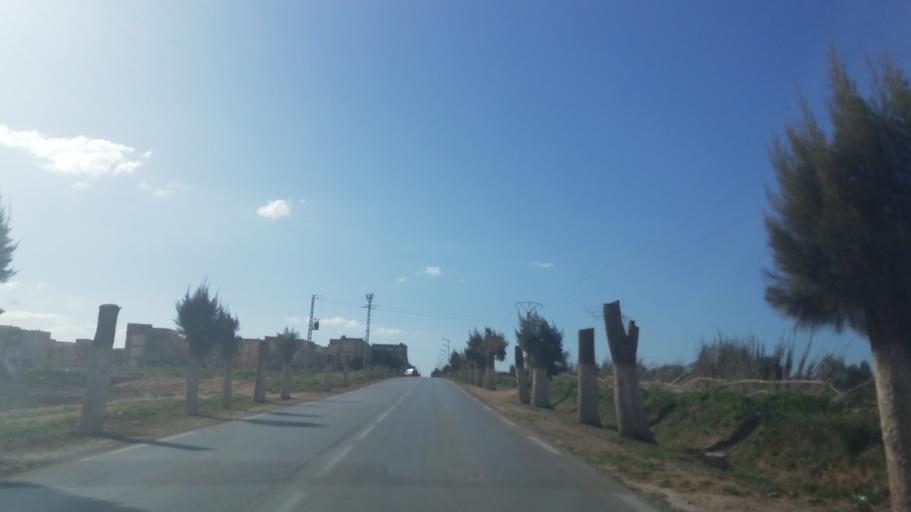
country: DZ
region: Mostaganem
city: Mostaganem
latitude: 35.9994
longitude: 0.3099
